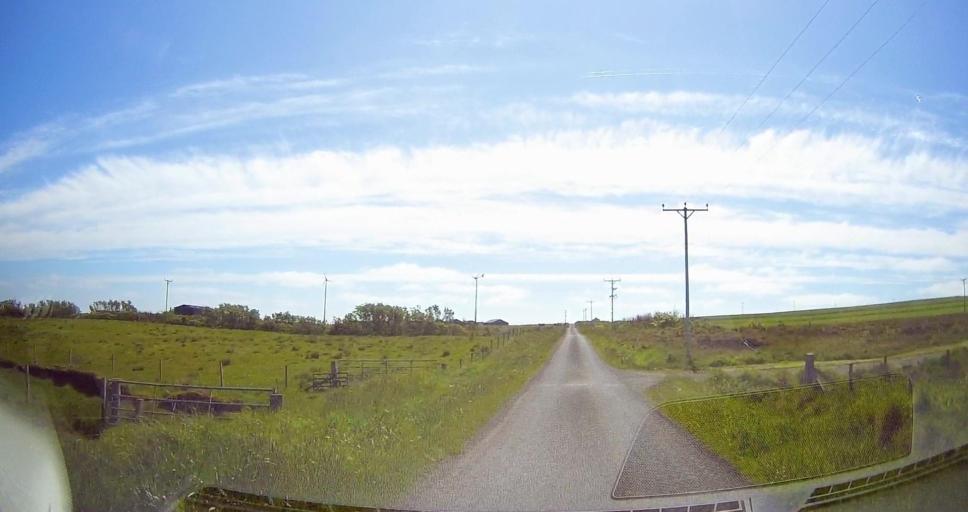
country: GB
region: Scotland
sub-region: Orkney Islands
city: Kirkwall
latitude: 58.8238
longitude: -2.9088
